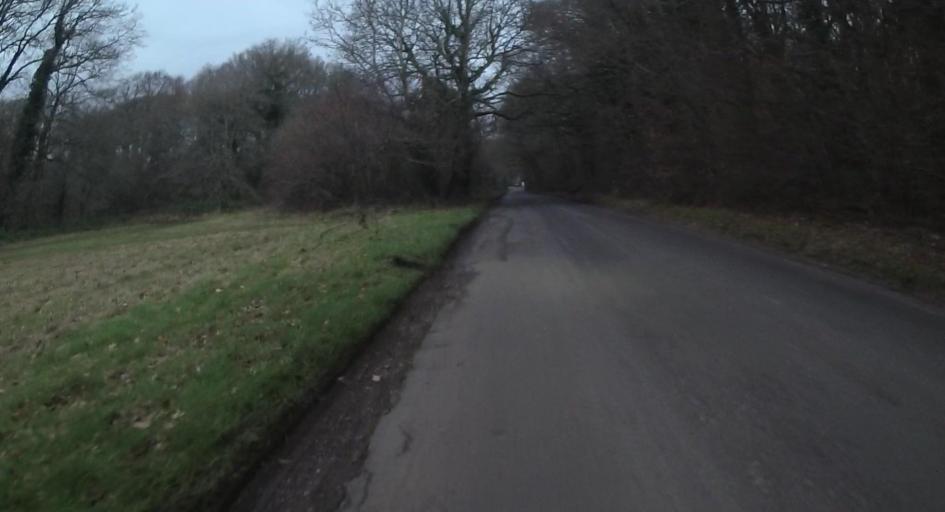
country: GB
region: England
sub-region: Hampshire
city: Four Marks
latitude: 51.0601
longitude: -1.1041
